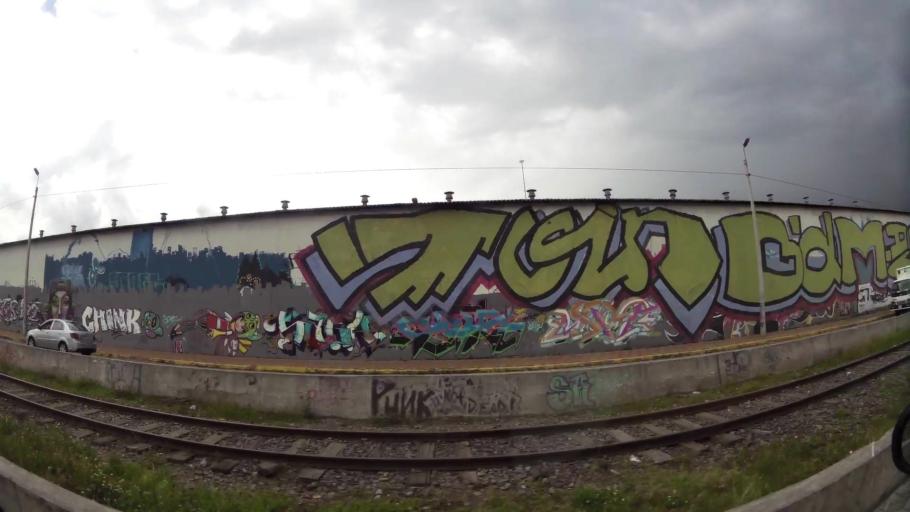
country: EC
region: Pichincha
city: Quito
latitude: -0.2878
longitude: -78.5382
